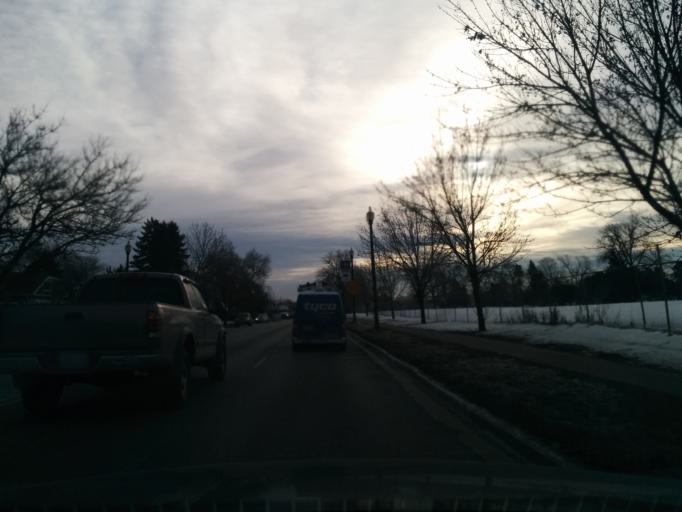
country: US
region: Illinois
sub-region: Cook County
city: Schiller Park
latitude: 41.9561
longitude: -87.8755
